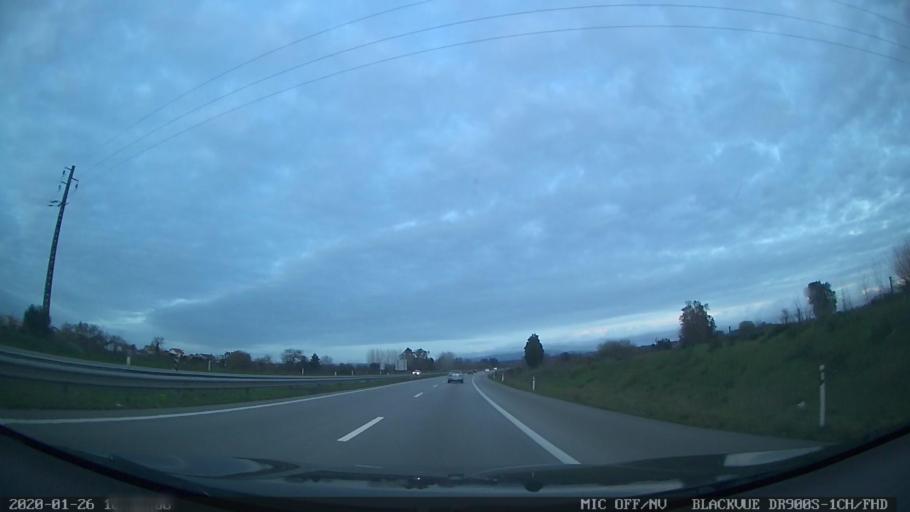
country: PT
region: Aveiro
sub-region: Aveiro
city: Eixo
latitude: 40.6684
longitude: -8.5868
